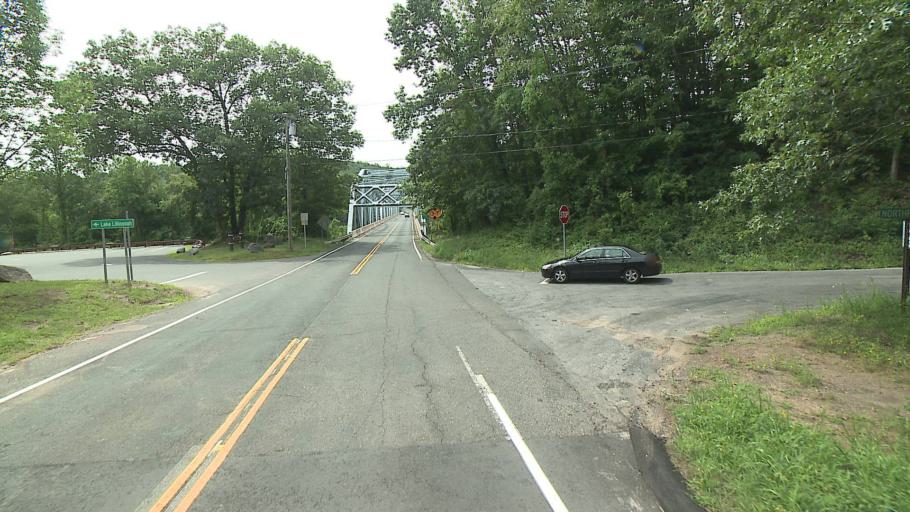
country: US
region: Connecticut
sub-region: Fairfield County
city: Newtown
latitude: 41.4812
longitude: -73.3505
